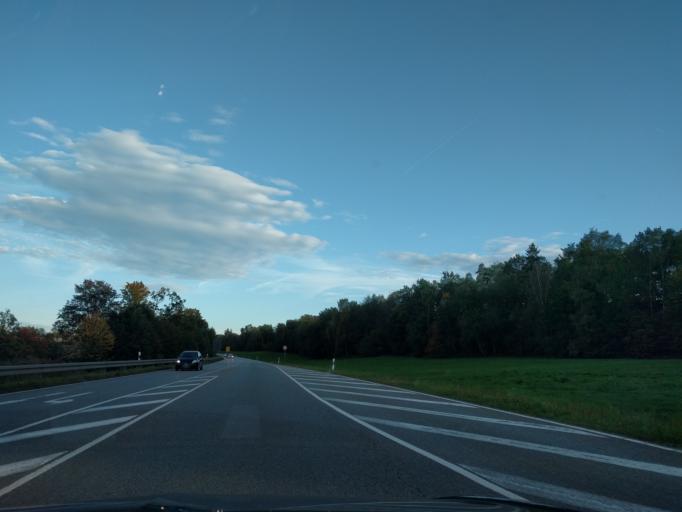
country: DE
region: Bavaria
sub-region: Lower Bavaria
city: Viechtach
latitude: 49.0743
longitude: 12.8803
